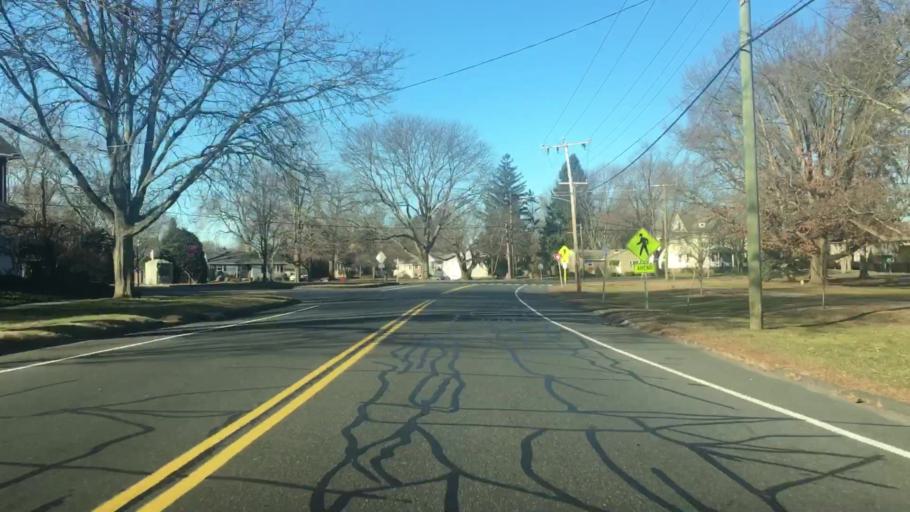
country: US
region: Connecticut
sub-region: Hartford County
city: Wethersfield
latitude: 41.7186
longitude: -72.6590
